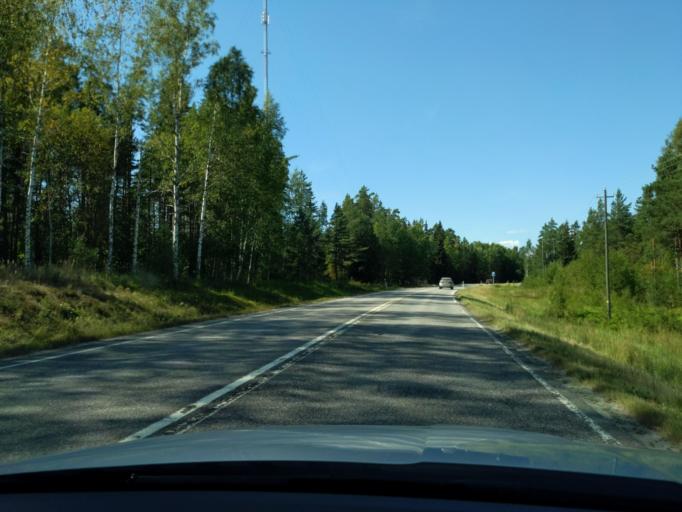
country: FI
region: Uusimaa
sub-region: Raaseporin
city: Ekenaes
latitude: 60.0182
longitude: 23.3804
